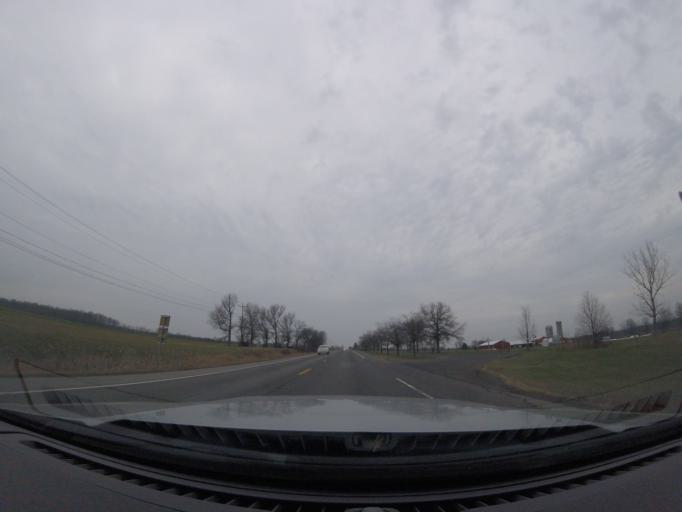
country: US
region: New York
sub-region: Yates County
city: Dundee
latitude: 42.6177
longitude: -76.9440
